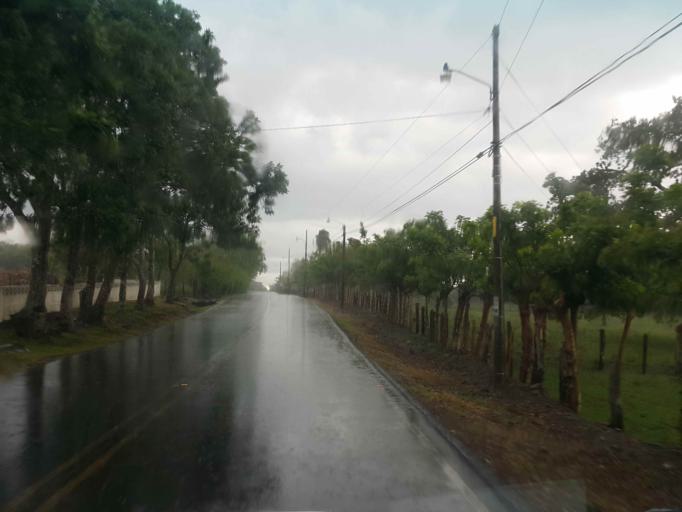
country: CR
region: Puntarenas
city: Miramar
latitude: 10.1214
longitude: -84.8297
